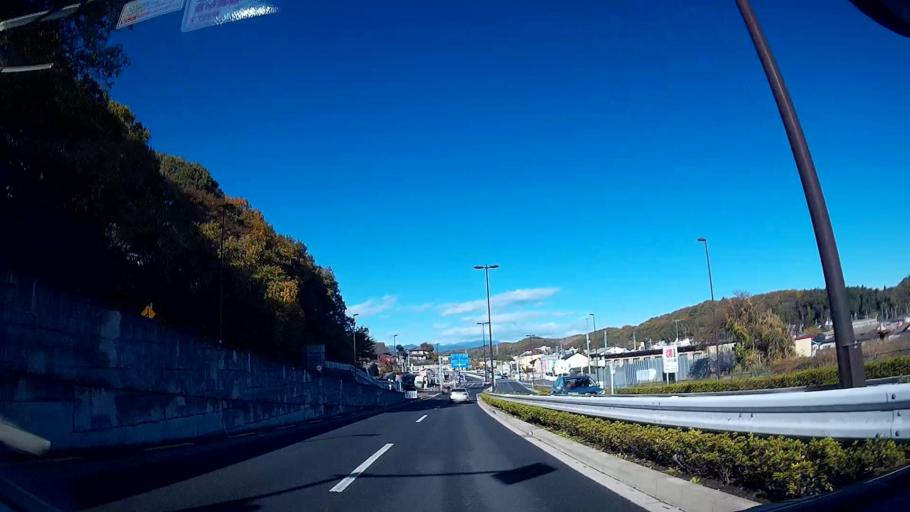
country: JP
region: Tokyo
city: Hachioji
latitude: 35.6944
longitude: 139.3240
